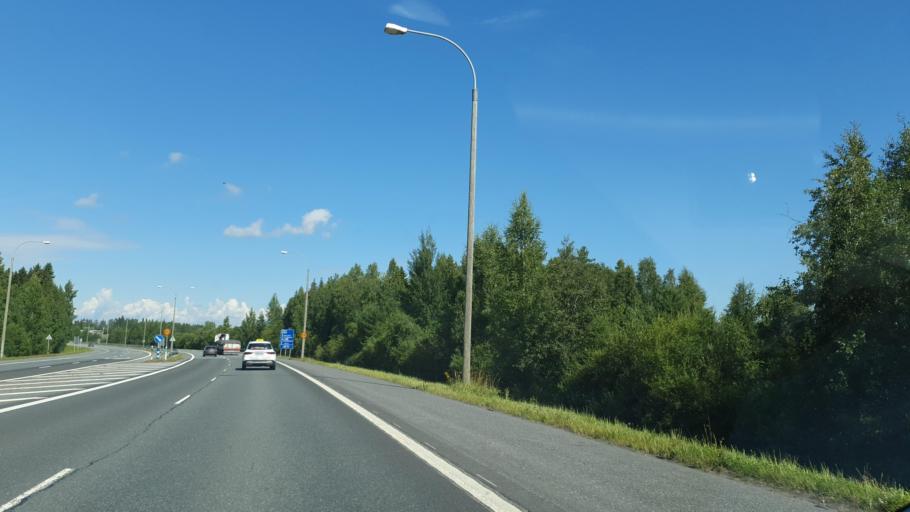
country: FI
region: Northern Savo
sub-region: Ylae-Savo
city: Iisalmi
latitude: 63.5155
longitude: 27.2573
